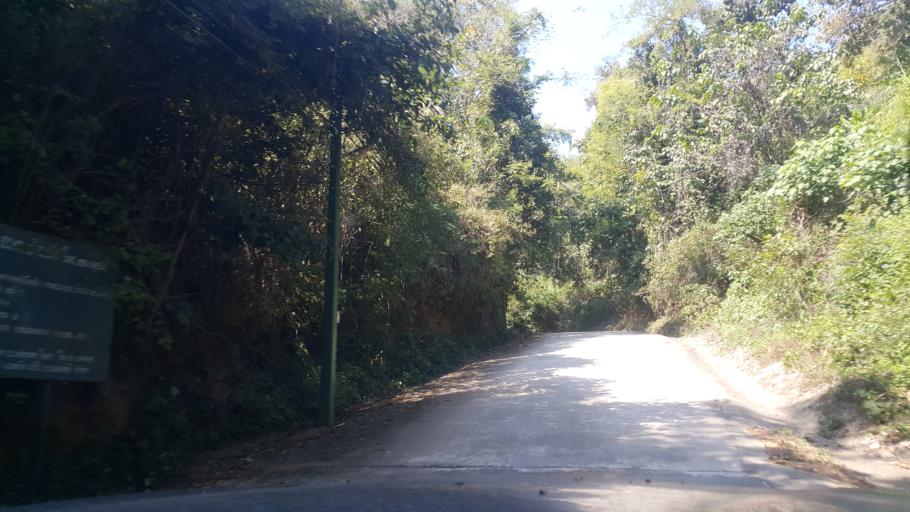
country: TH
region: Chiang Mai
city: Hang Dong
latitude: 18.7495
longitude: 98.8790
